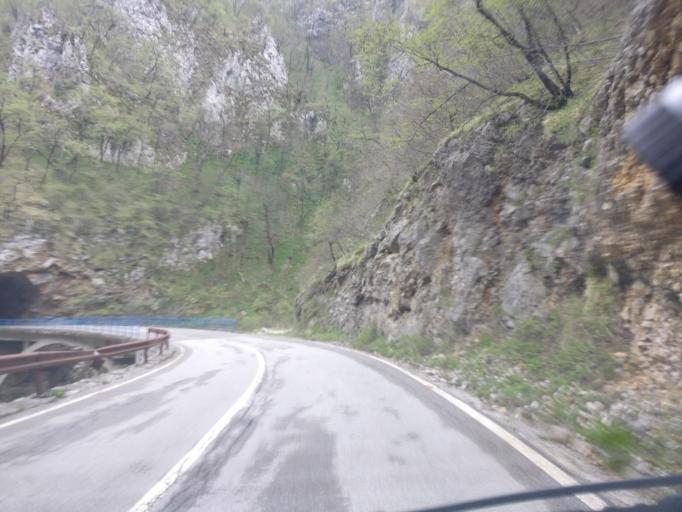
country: ME
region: Opstina Pluzine
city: Pluzine
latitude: 43.2929
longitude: 18.8503
